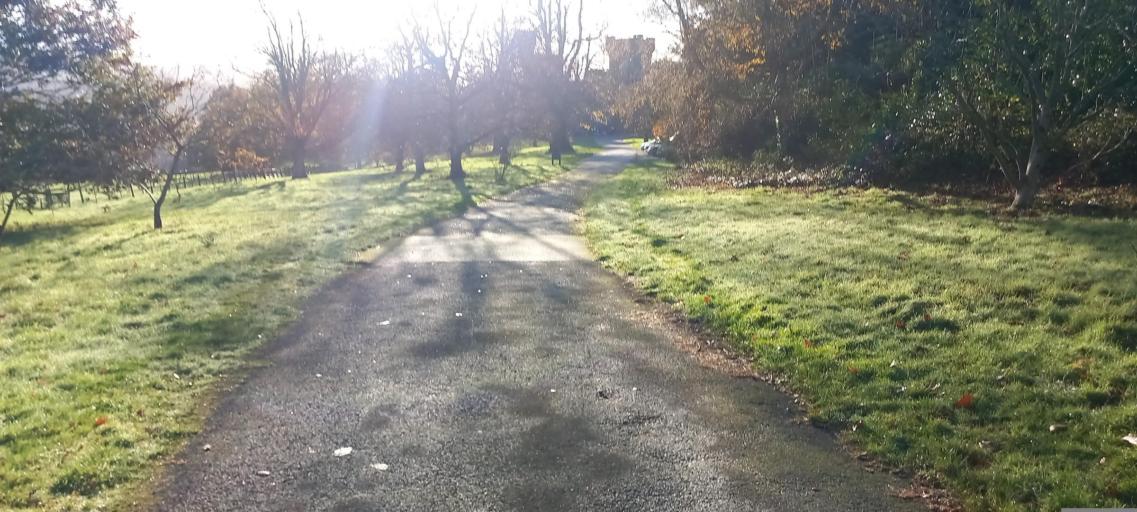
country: GB
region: Wales
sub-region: Anglesey
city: Beaumaris
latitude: 53.2283
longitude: -4.0952
